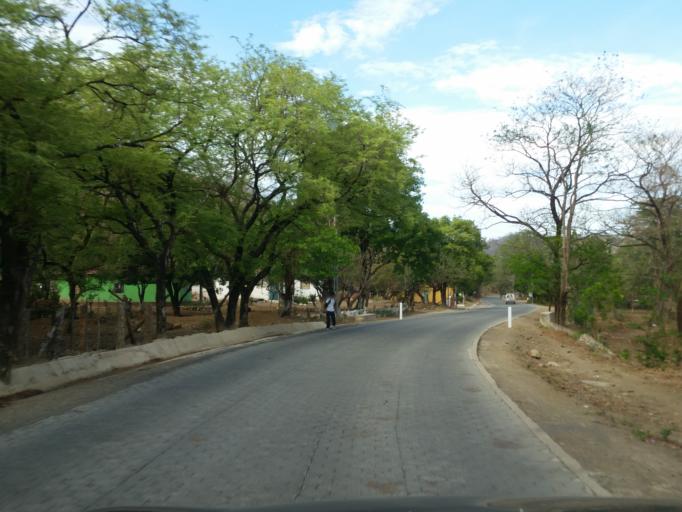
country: NI
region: Rivas
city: Tola
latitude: 11.3917
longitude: -85.9757
